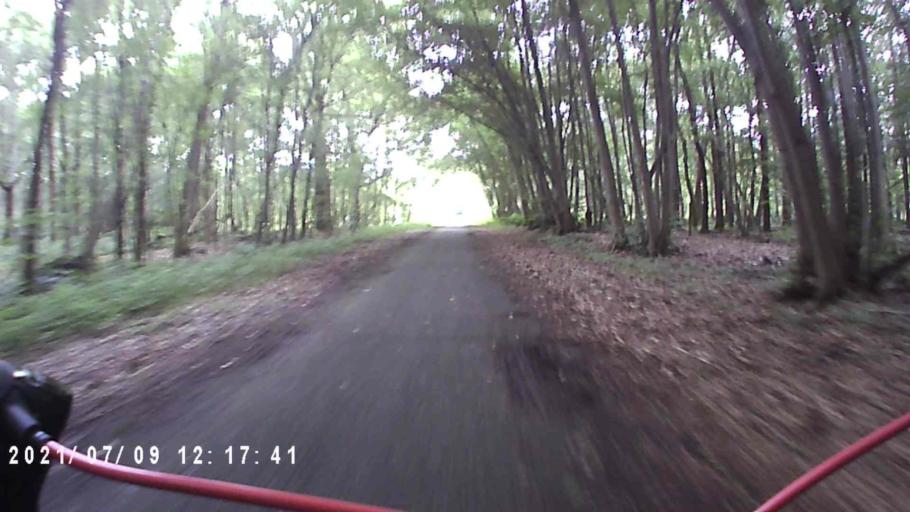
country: NL
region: Groningen
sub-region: Gemeente  Oldambt
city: Winschoten
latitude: 53.1754
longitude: 6.9998
